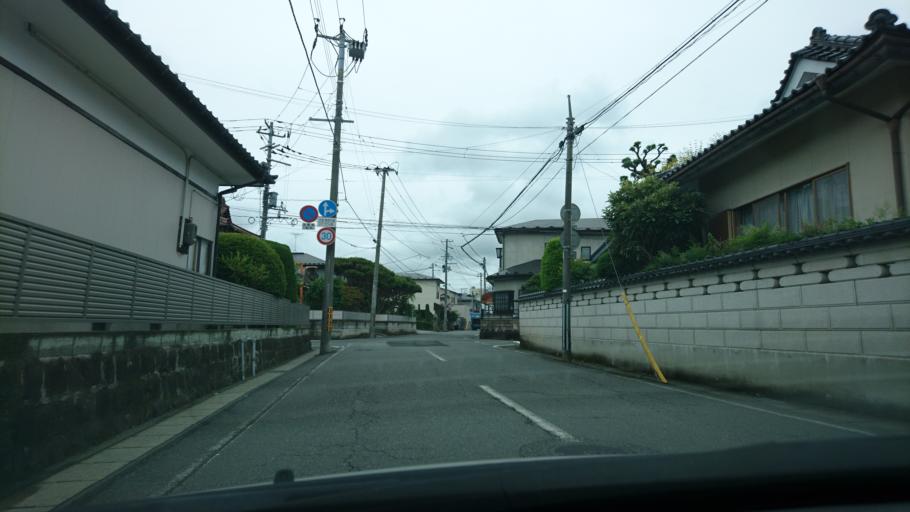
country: JP
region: Iwate
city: Ichinoseki
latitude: 38.9333
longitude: 141.1383
